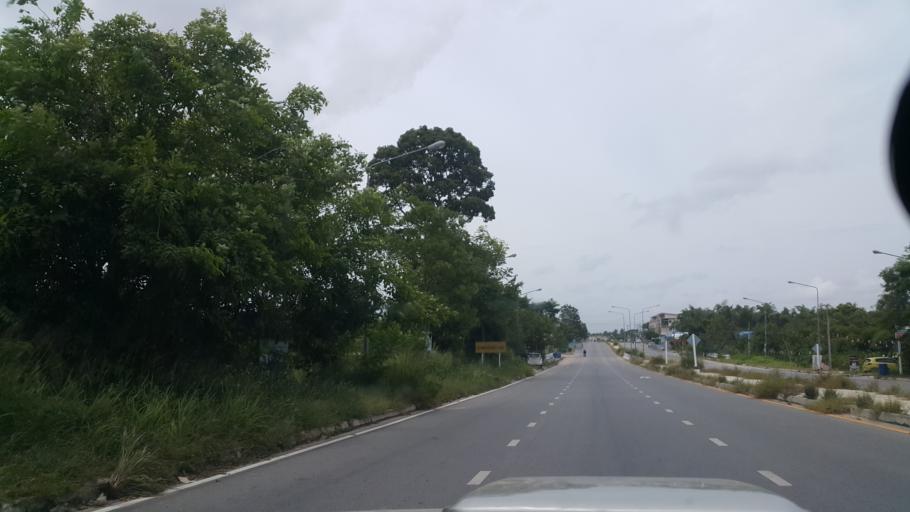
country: TH
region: Rayong
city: Ban Chang
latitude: 12.7149
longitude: 101.0594
